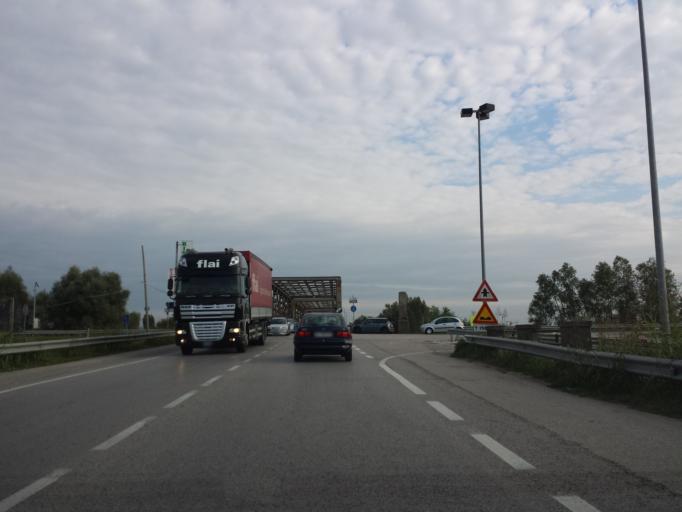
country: IT
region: Veneto
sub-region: Provincia di Padova
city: Boara Pisani
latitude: 45.1062
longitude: 11.7832
